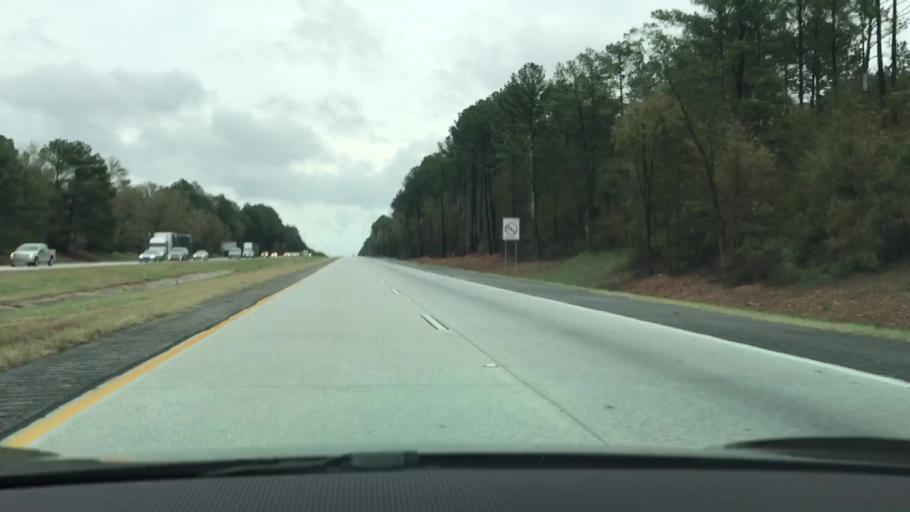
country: US
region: Georgia
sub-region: Taliaferro County
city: Crawfordville
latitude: 33.5281
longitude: -82.8963
